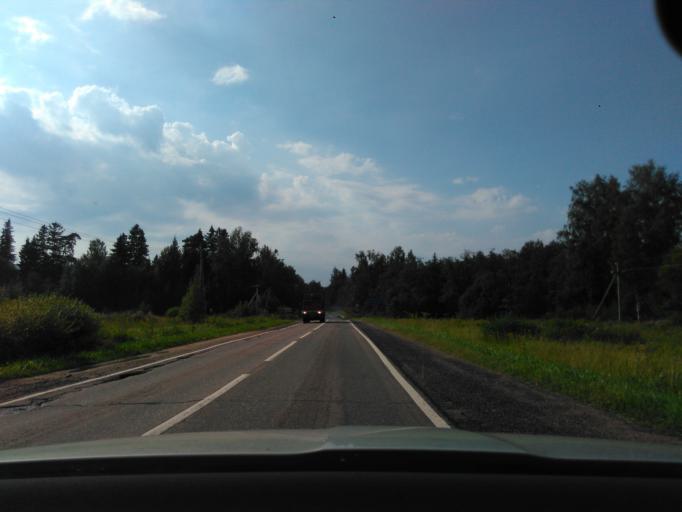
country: RU
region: Moskovskaya
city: Solnechnogorsk
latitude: 56.1413
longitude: 36.8370
